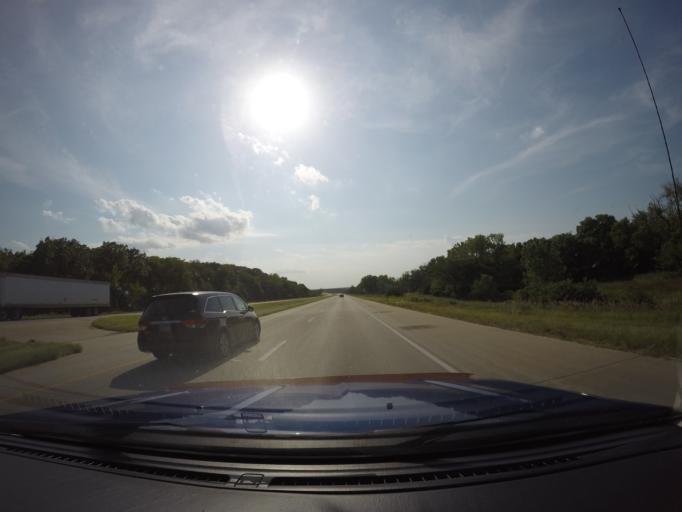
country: US
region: Kansas
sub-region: Riley County
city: Manhattan
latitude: 39.0673
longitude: -96.4645
